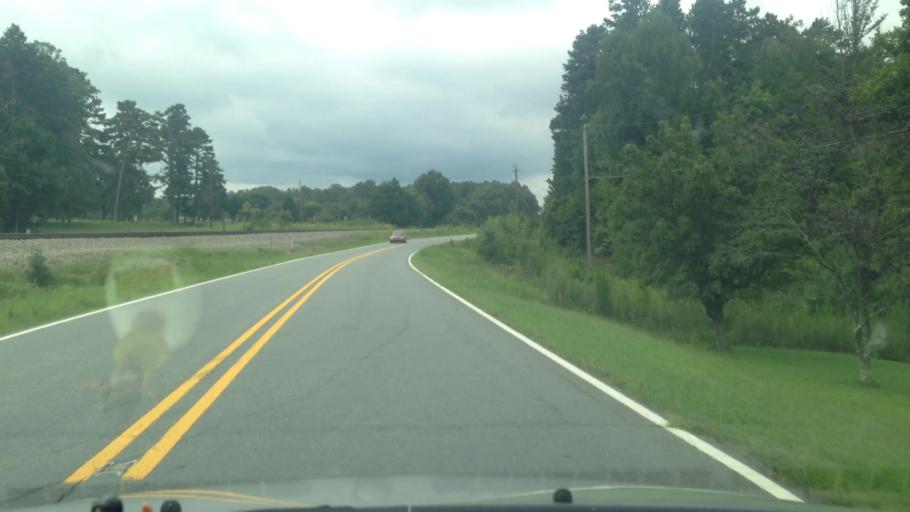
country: US
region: North Carolina
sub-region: Stokes County
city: Walnut Cove
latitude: 36.2556
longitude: -80.1480
